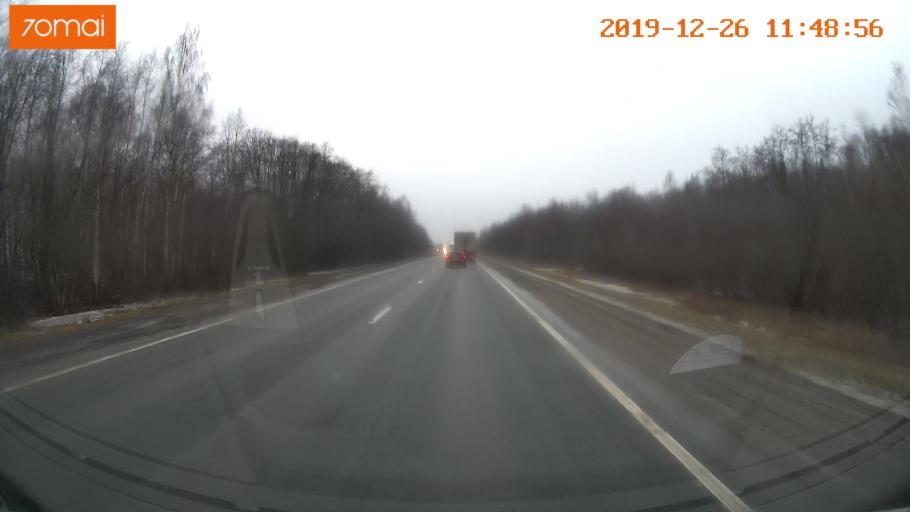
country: RU
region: Vologda
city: Sheksna
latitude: 59.2449
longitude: 38.4281
